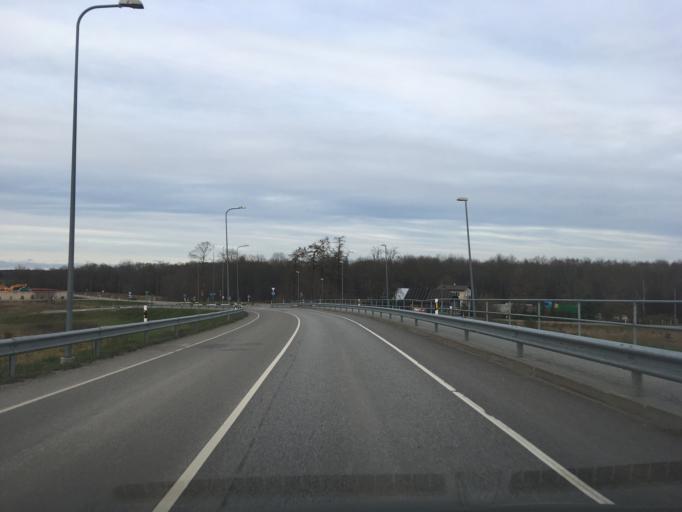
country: EE
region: Ida-Virumaa
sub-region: Johvi vald
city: Johvi
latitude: 59.3696
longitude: 27.3914
